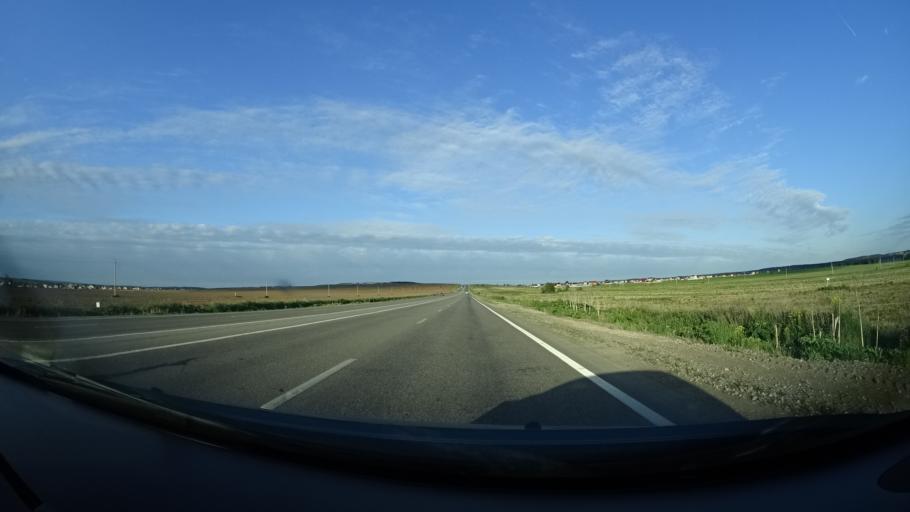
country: RU
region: Perm
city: Kultayevo
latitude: 57.8802
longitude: 55.9132
